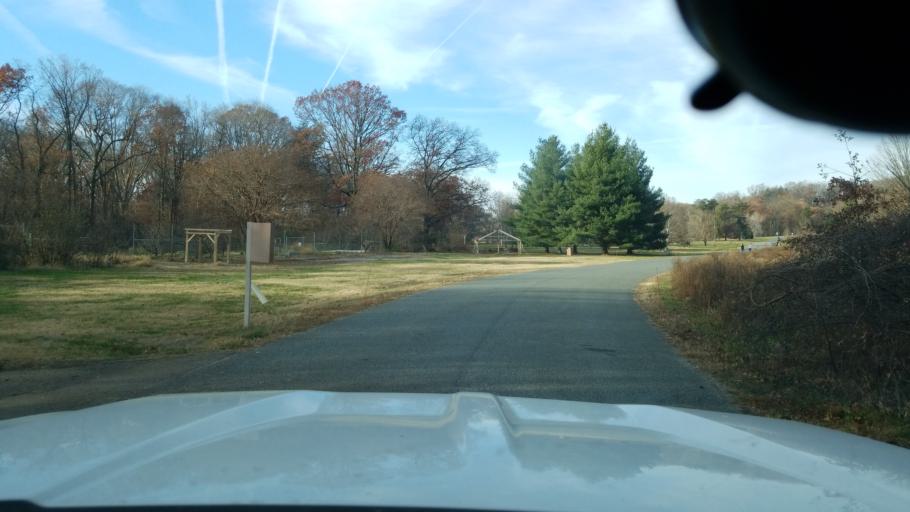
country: US
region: Maryland
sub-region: Prince George's County
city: Colmar Manor
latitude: 38.9082
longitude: -76.9644
